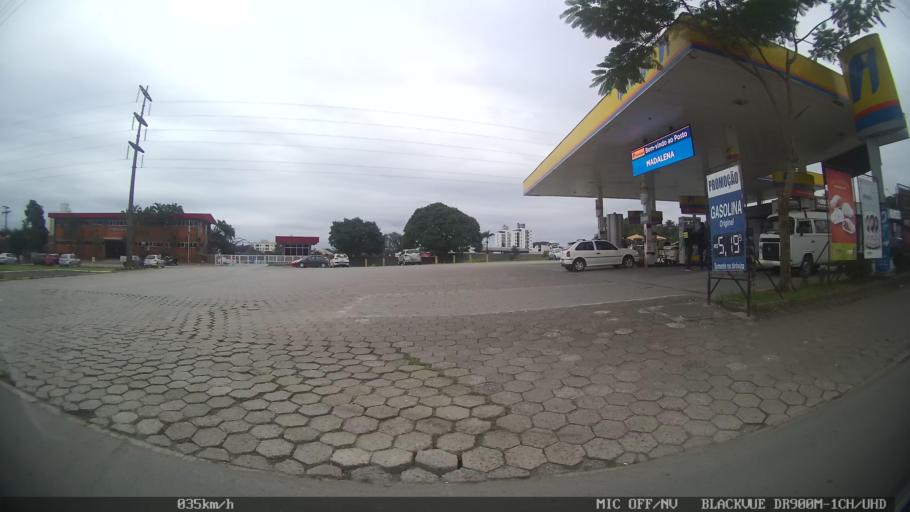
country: BR
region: Santa Catarina
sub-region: Joinville
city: Joinville
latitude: -26.2741
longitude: -48.8686
